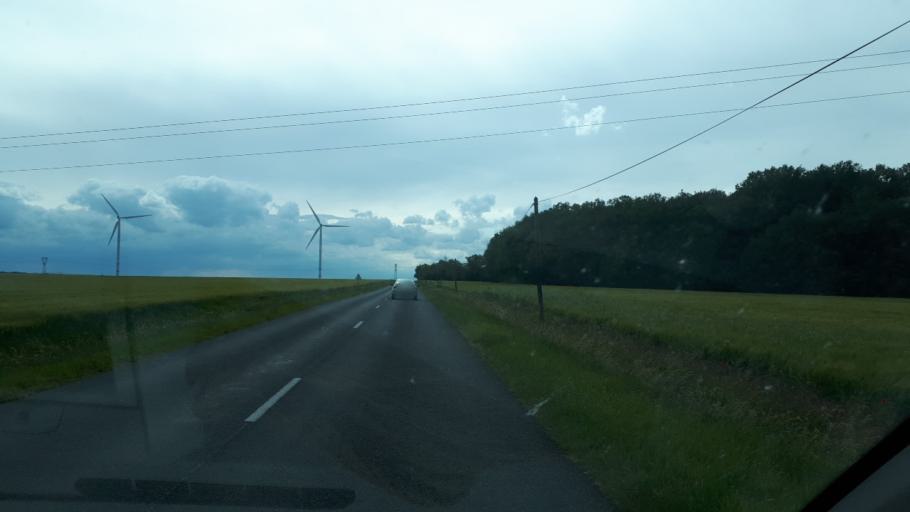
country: FR
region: Centre
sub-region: Departement du Cher
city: Marmagne
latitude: 47.0810
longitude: 2.2520
